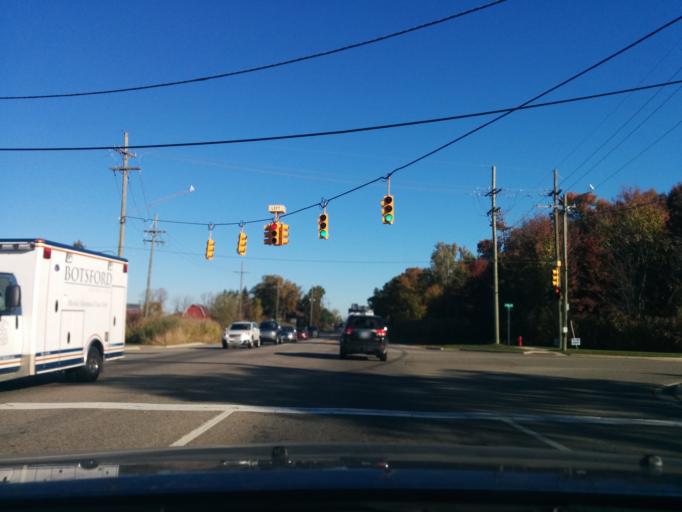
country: US
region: Michigan
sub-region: Oakland County
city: Novi
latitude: 42.4796
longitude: -83.5151
